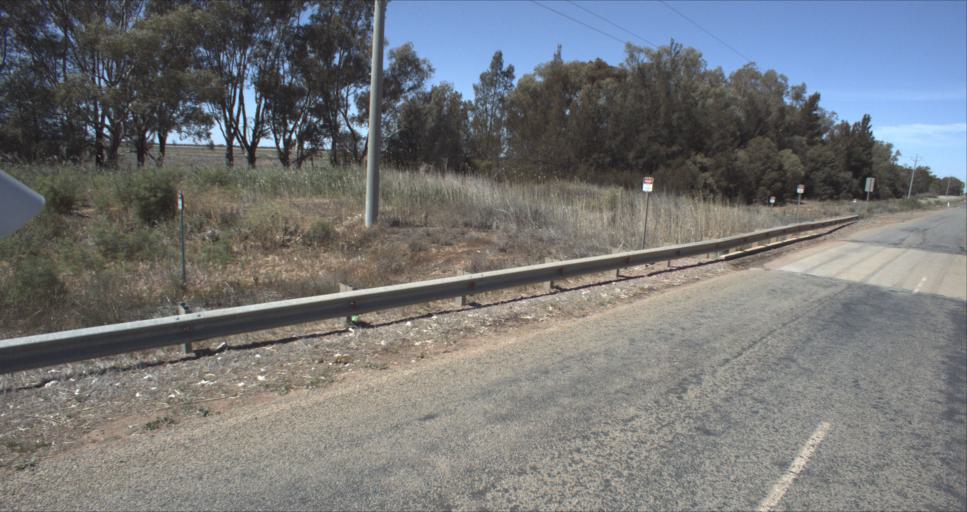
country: AU
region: New South Wales
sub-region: Leeton
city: Leeton
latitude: -34.4646
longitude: 146.2935
